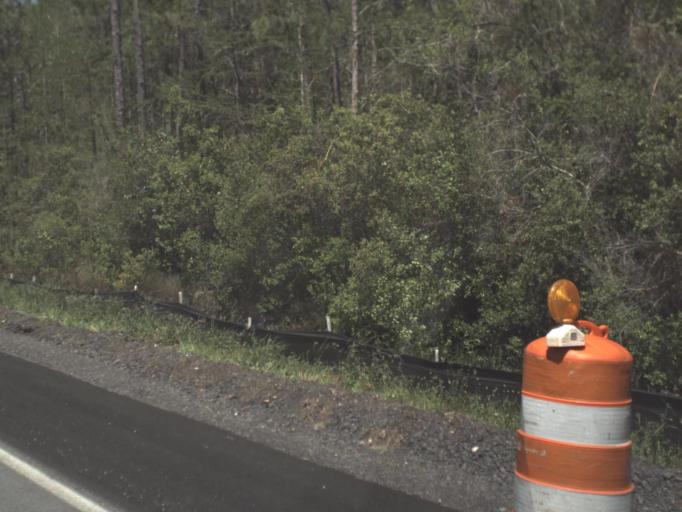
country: US
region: Florida
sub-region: Escambia County
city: Myrtle Grove
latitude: 30.3998
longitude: -87.3178
